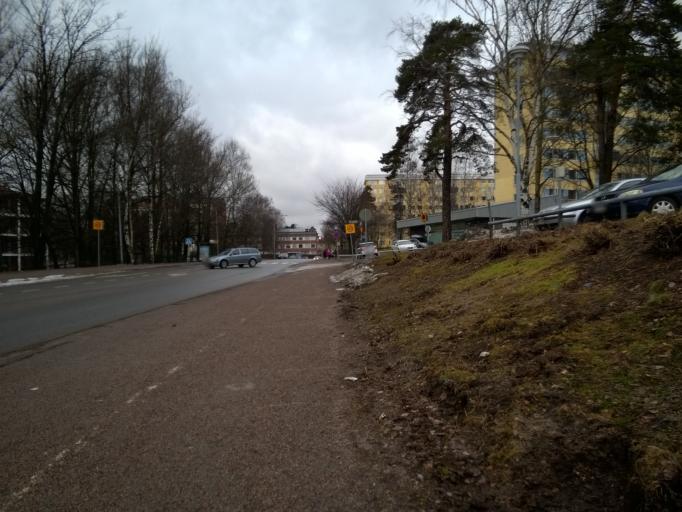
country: FI
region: Uusimaa
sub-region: Helsinki
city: Helsinki
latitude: 60.2163
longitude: 24.9682
